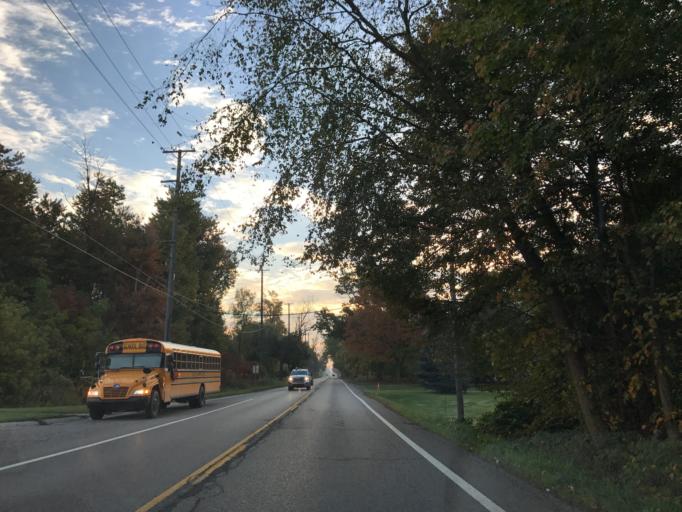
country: US
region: Michigan
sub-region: Oakland County
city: South Lyon
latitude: 42.4622
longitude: -83.6066
